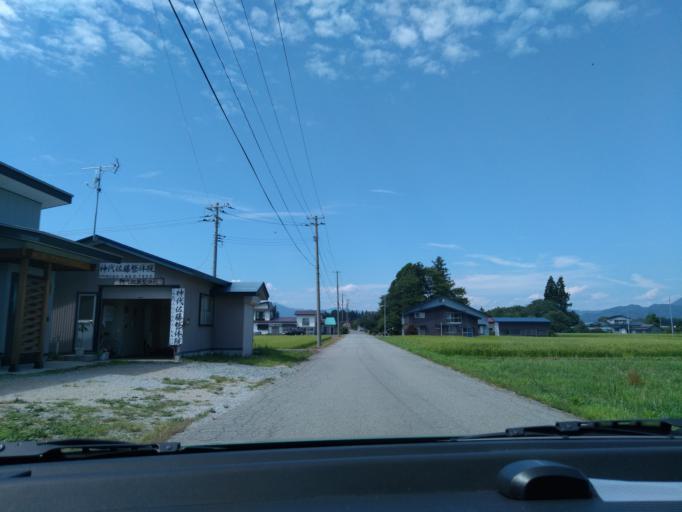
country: JP
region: Akita
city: Kakunodatemachi
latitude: 39.6060
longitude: 140.5957
